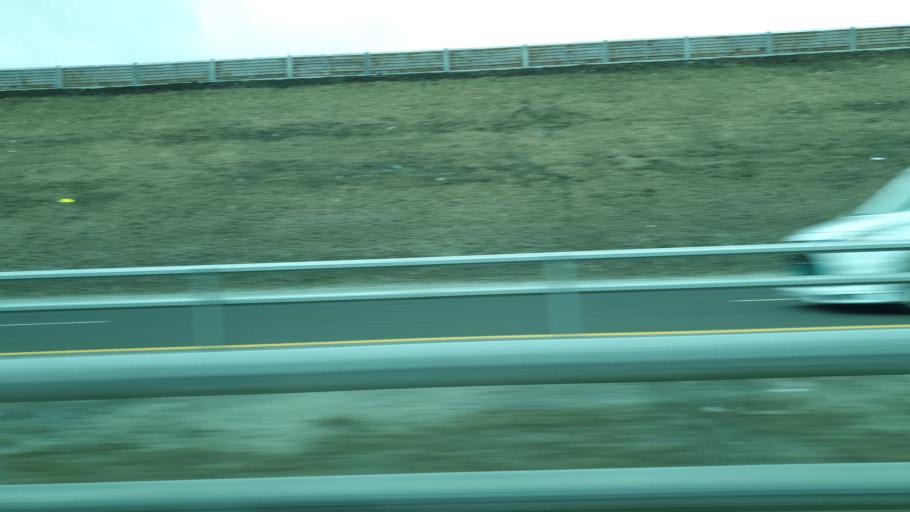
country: NO
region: Sor-Trondelag
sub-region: Trondheim
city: Trondheim
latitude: 63.3519
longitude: 10.3707
